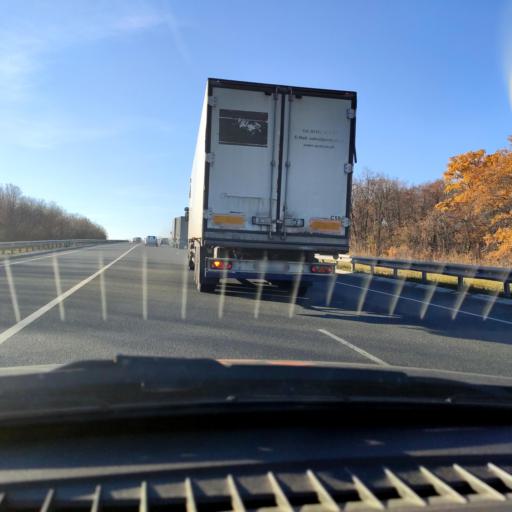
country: RU
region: Samara
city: Mezhdurechensk
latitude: 53.2590
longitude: 49.0917
